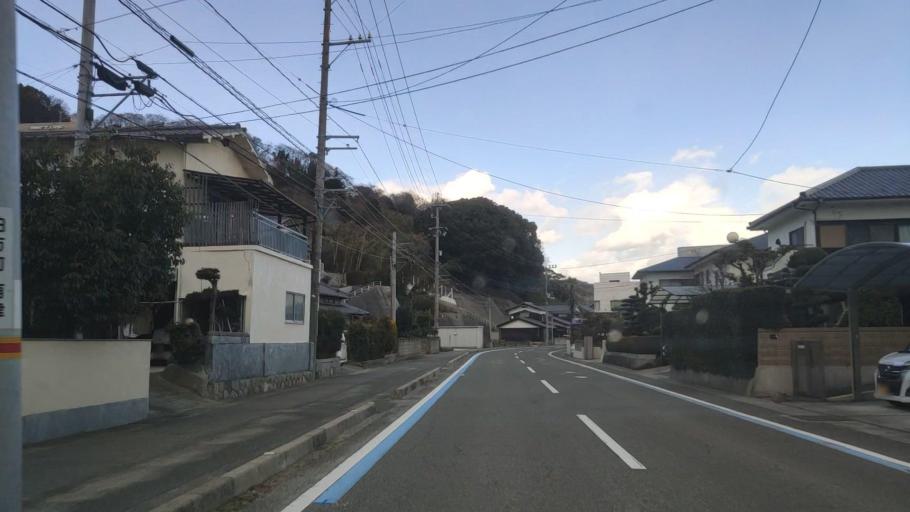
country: JP
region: Hiroshima
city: Innoshima
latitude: 34.2005
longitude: 133.0900
